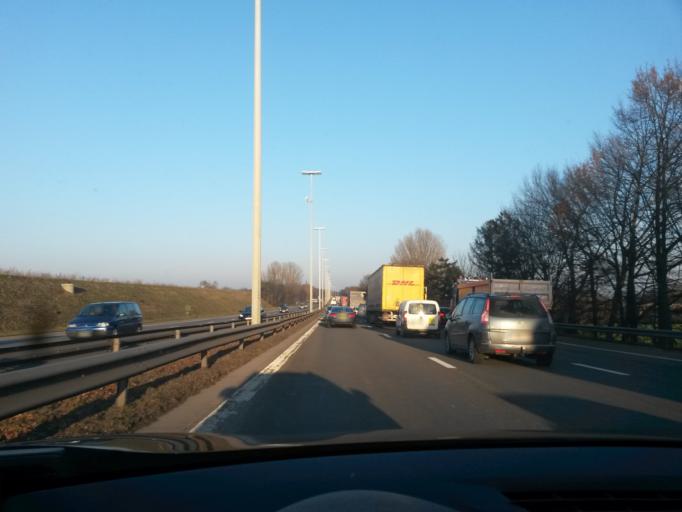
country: BE
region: Wallonia
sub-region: Province de Liege
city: Herstal
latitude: 50.6836
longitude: 5.6003
